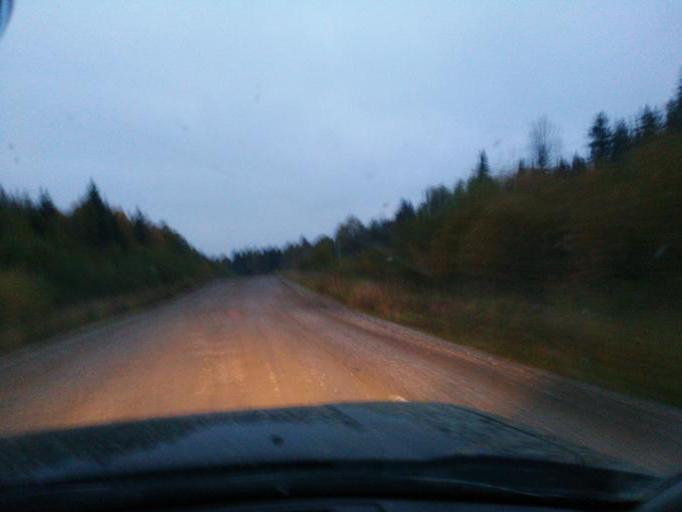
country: RU
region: Perm
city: Gornozavodsk
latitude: 57.9055
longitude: 58.3847
